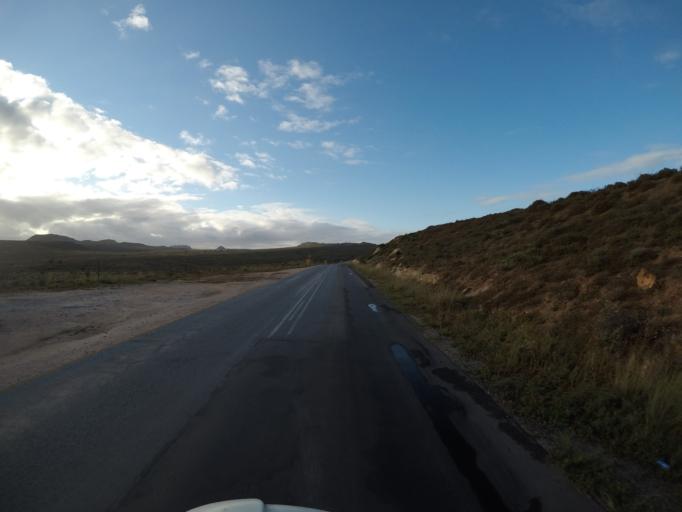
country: ZA
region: Western Cape
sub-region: West Coast District Municipality
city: Clanwilliam
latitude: -32.3298
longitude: 18.3707
